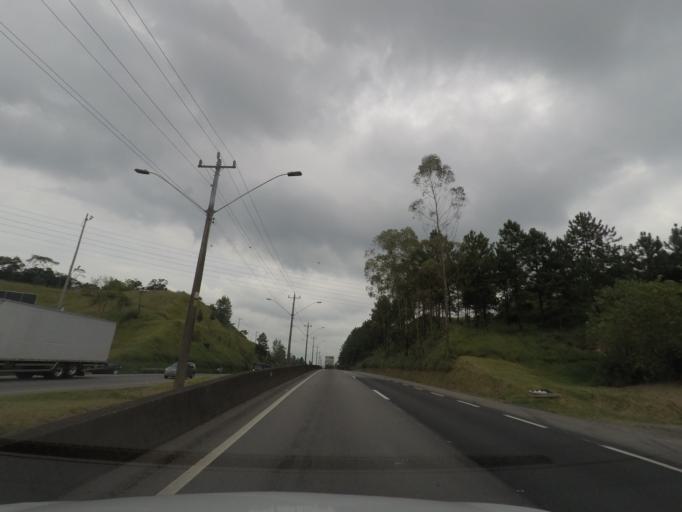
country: BR
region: Sao Paulo
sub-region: Sao Lourenco Da Serra
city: Sao Lourenco da Serra
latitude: -23.8670
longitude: -46.9527
